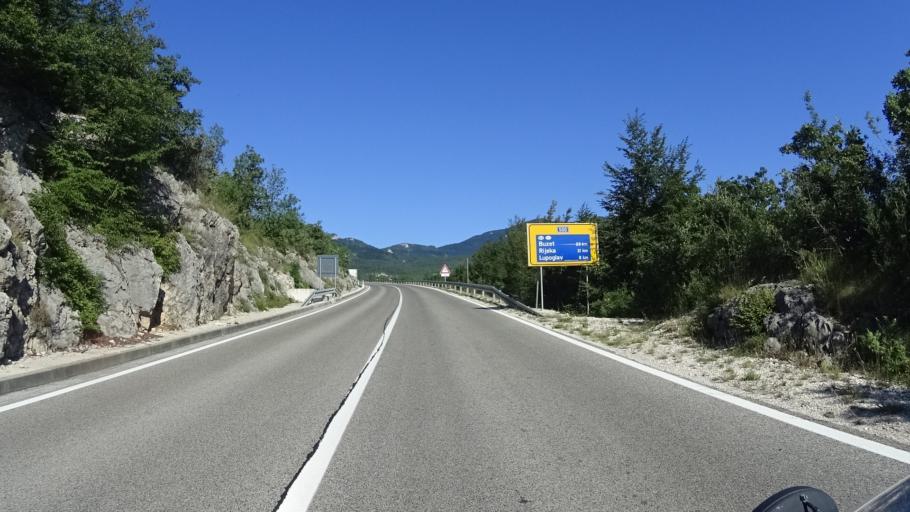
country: HR
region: Istarska
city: Lovran
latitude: 45.3225
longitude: 14.1508
